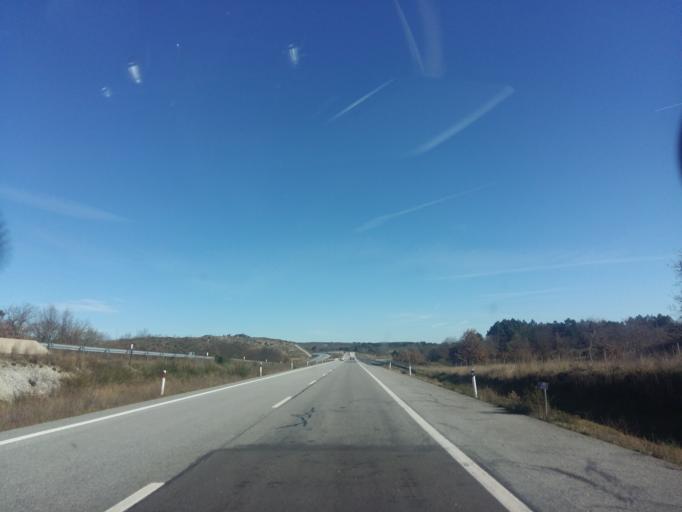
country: PT
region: Guarda
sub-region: Guarda
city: Sequeira
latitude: 40.5810
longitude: -7.1646
